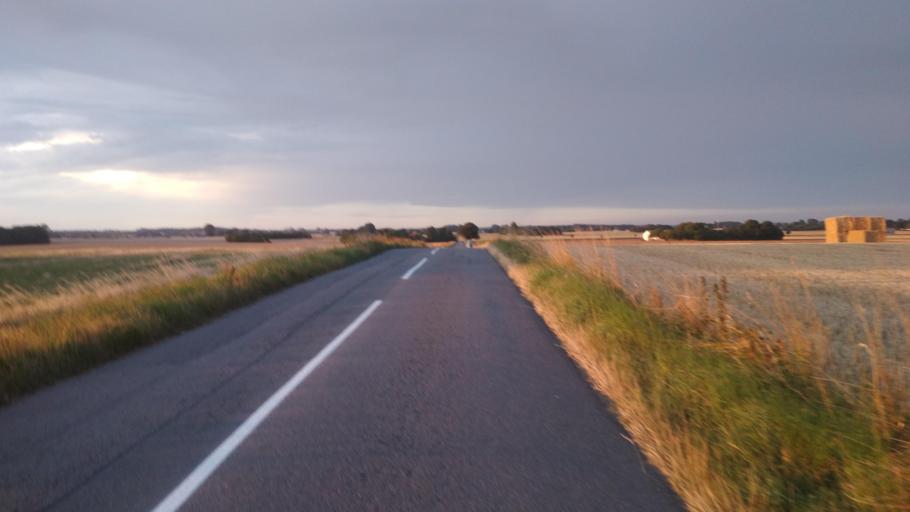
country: DK
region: Capital Region
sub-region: Bornholm Kommune
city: Akirkeby
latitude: 55.0290
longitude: 14.9114
